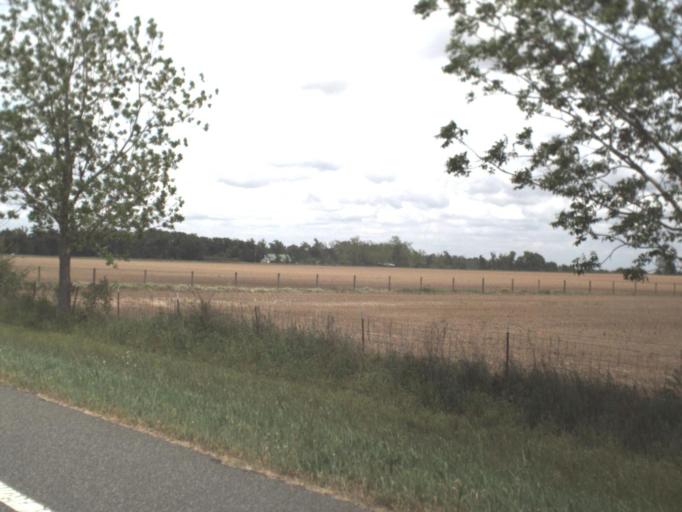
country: US
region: Florida
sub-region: Santa Rosa County
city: Point Baker
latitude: 30.7986
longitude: -87.0921
